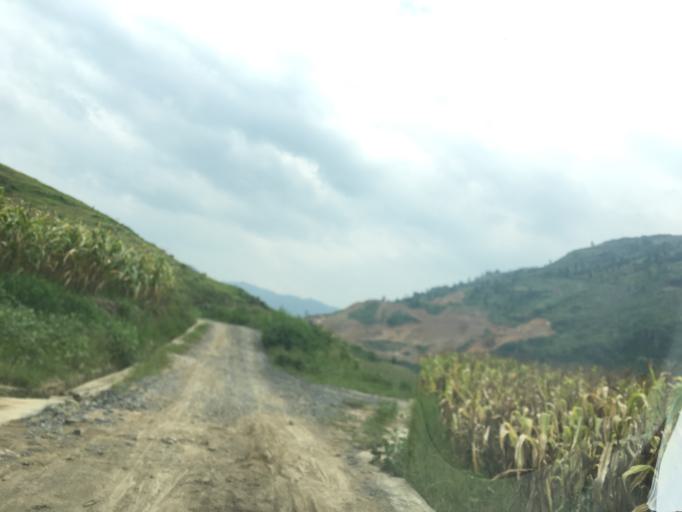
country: CN
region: Guangxi Zhuangzu Zizhiqu
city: Xinzhou
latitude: 25.1822
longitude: 105.7313
